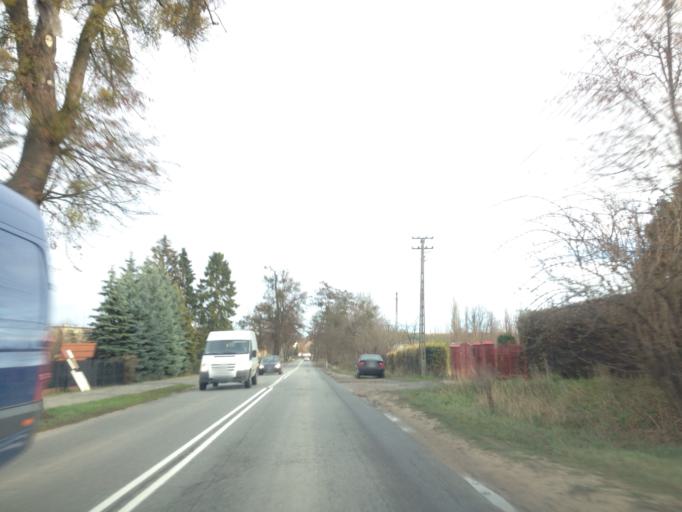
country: PL
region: Pomeranian Voivodeship
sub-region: Powiat gdanski
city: Lublewo Gdanskie
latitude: 54.2849
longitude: 18.5047
